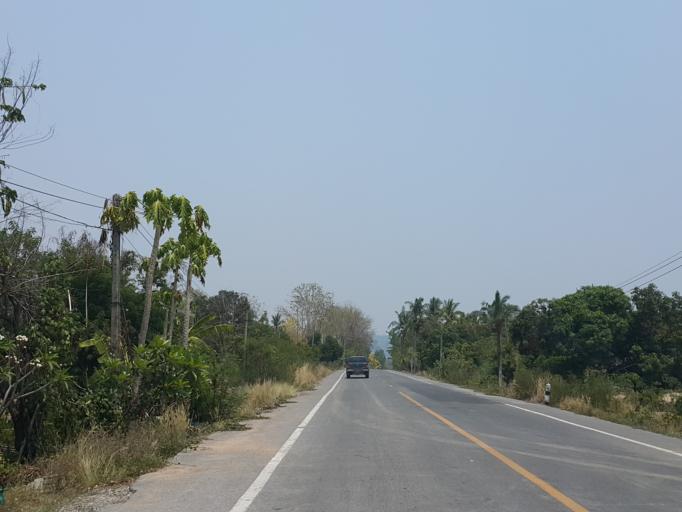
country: TH
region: Kamphaeng Phet
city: Pang Sila Thong
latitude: 16.0544
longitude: 99.3530
